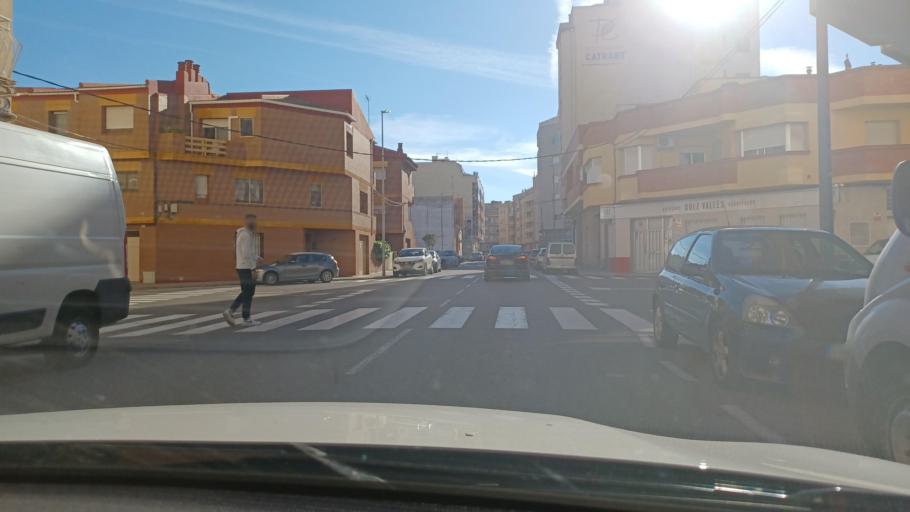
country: ES
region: Catalonia
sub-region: Provincia de Tarragona
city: Amposta
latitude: 40.7045
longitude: 0.5804
